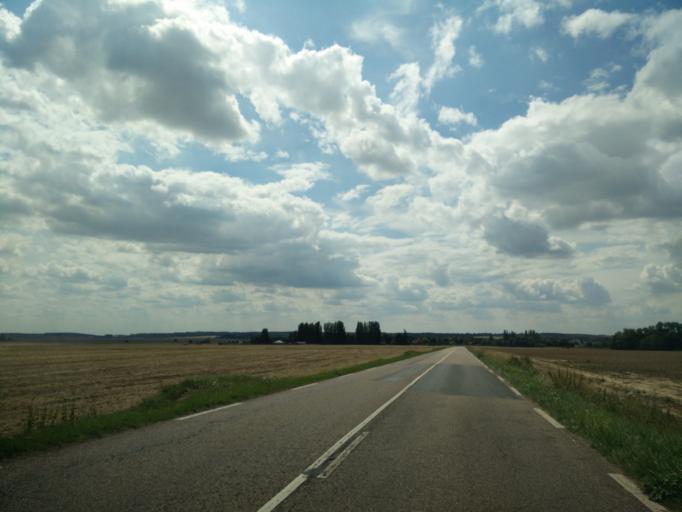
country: FR
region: Ile-de-France
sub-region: Departement des Yvelines
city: Guerville
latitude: 48.9225
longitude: 1.7318
